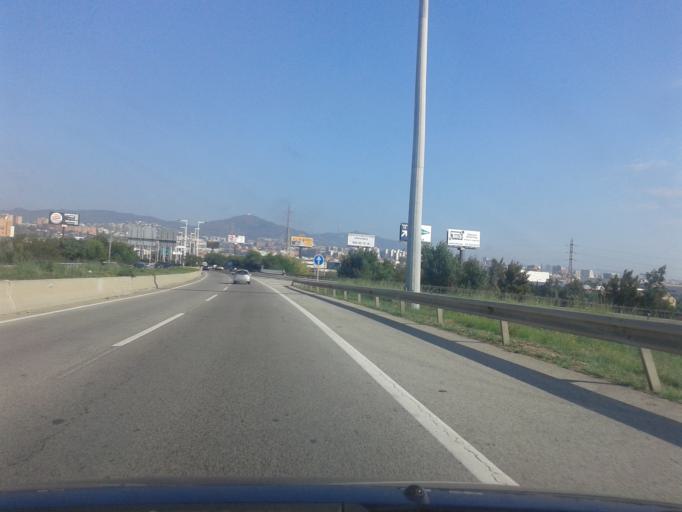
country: ES
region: Catalonia
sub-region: Provincia de Barcelona
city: Cornella de Llobregat
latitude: 41.3467
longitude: 2.0923
